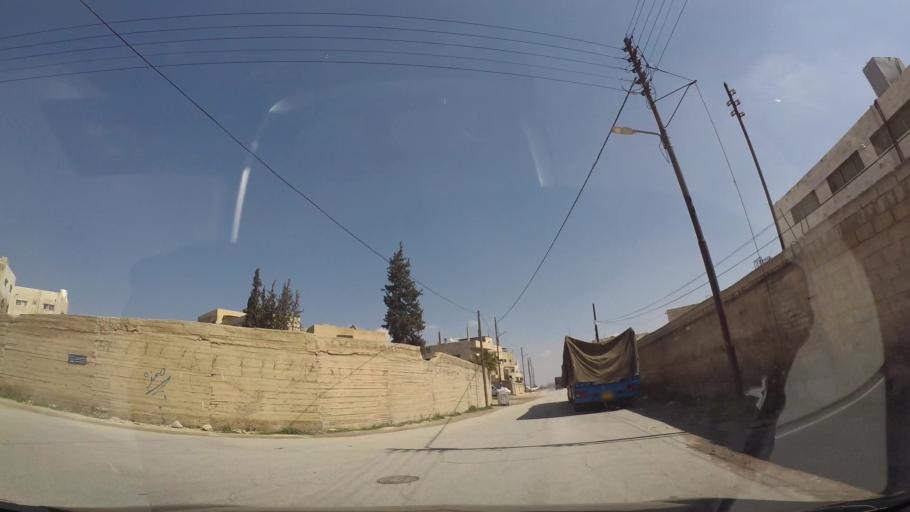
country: JO
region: Amman
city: Amman
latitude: 31.9822
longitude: 35.9953
